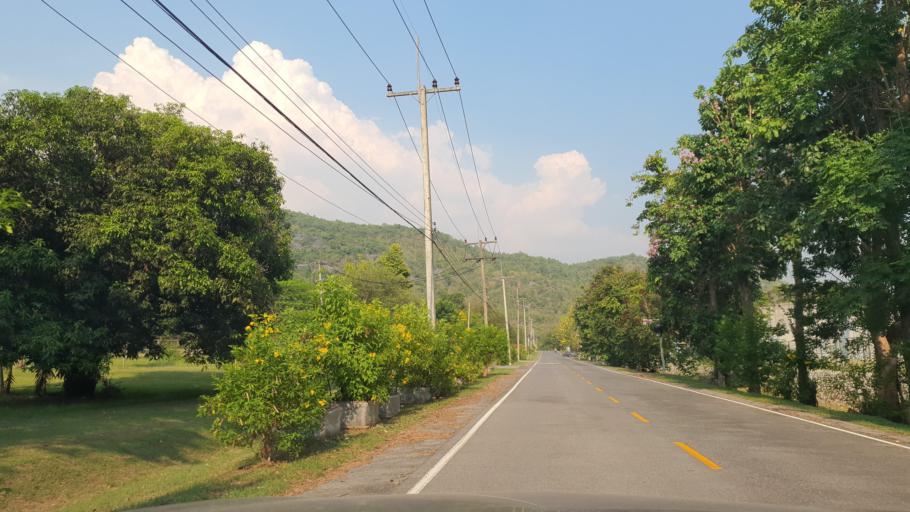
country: TH
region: Kanchanaburi
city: Sai Yok
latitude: 14.2299
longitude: 99.2334
